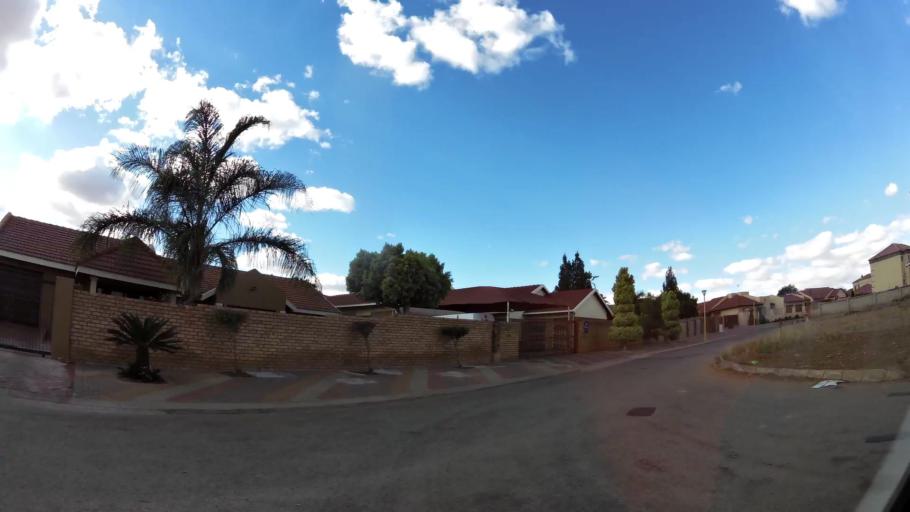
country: ZA
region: Limpopo
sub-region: Capricorn District Municipality
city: Polokwane
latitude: -23.9139
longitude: 29.5025
